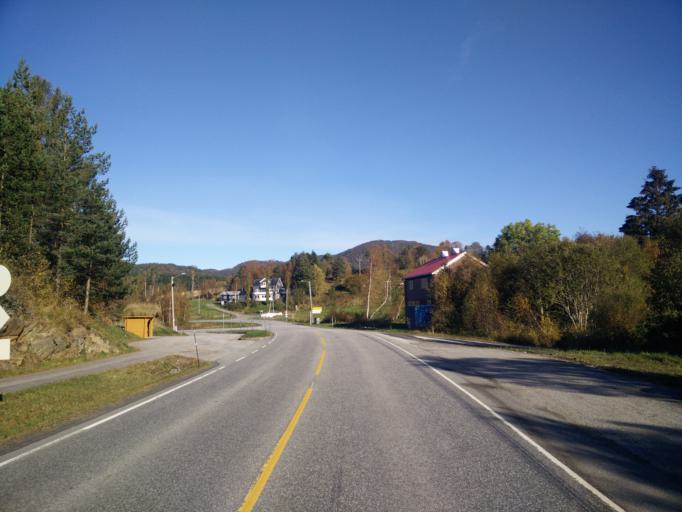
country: NO
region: More og Romsdal
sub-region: Tingvoll
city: Tingvoll
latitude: 63.0389
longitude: 8.0450
